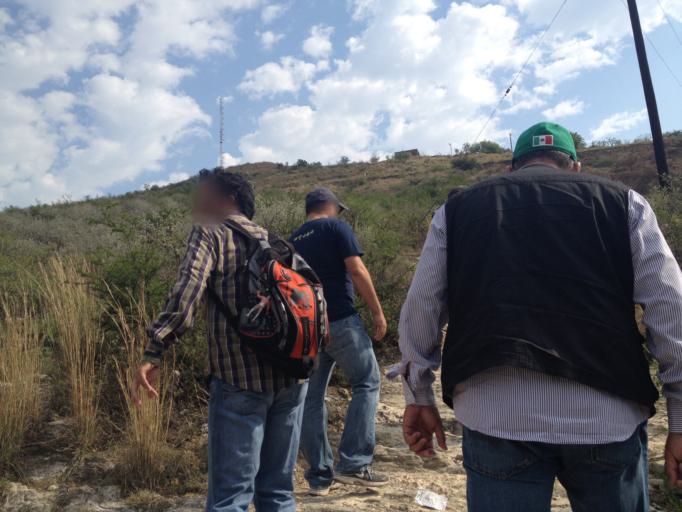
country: MX
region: Nuevo Leon
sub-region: Monterrey
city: Monterrey
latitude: 25.6533
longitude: -100.3316
